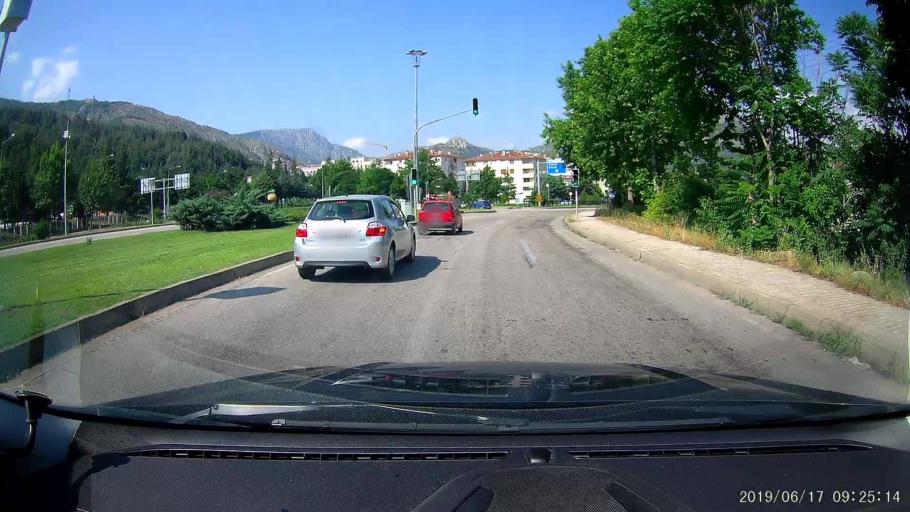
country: TR
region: Amasya
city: Amasya
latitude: 40.6678
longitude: 35.8511
